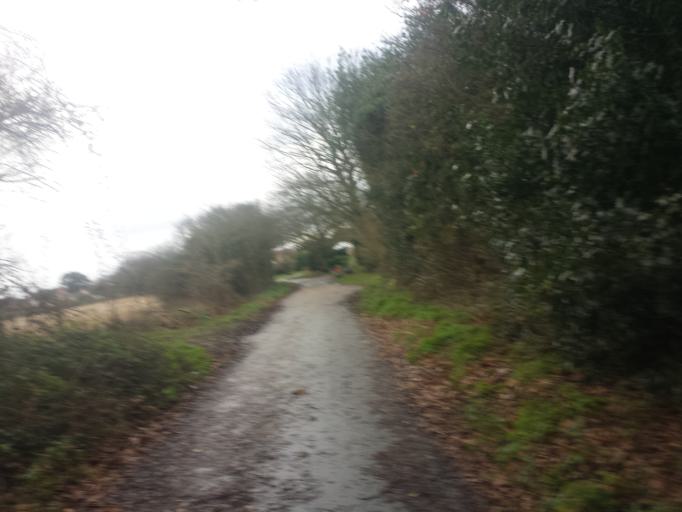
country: GB
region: England
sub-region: Essex
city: Great Bentley
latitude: 51.8841
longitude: 1.0366
